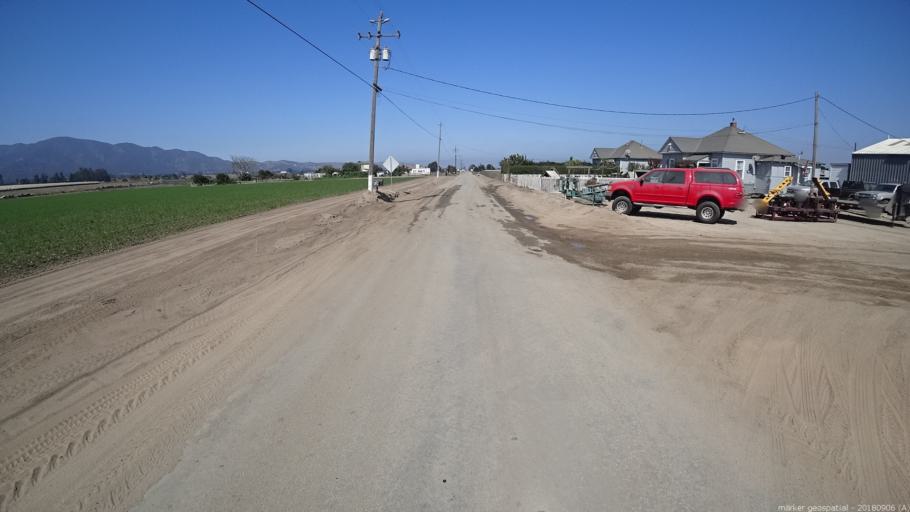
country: US
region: California
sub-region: Monterey County
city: Chualar
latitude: 36.5958
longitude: -121.6020
